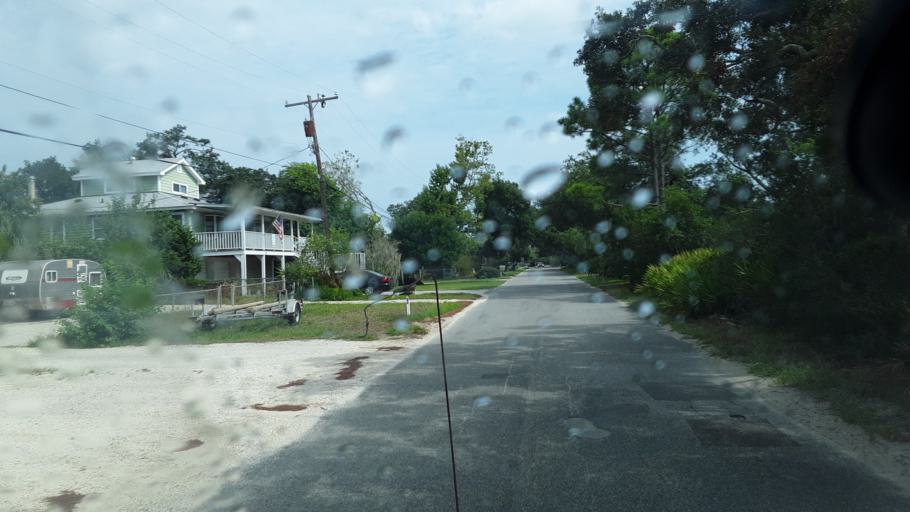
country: US
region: Georgia
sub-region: Chatham County
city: Tybee Island
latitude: 32.0136
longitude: -80.8679
